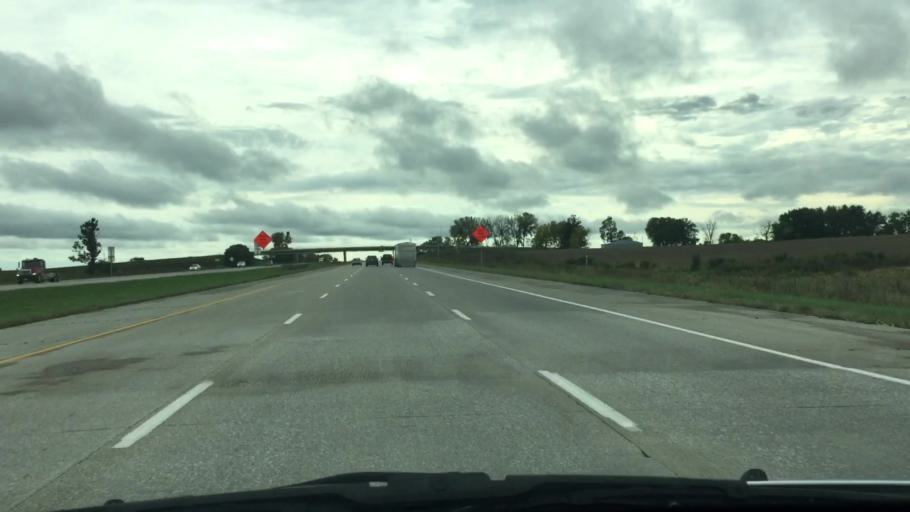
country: US
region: Iowa
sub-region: Polk County
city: West Des Moines
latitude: 41.5097
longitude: -93.7806
